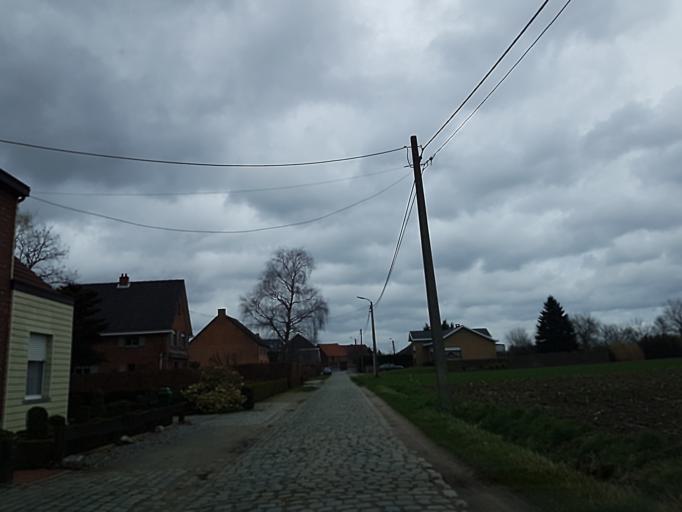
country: BE
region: Flanders
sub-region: Provincie Vlaams-Brabant
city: Zemst
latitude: 51.0041
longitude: 4.4167
